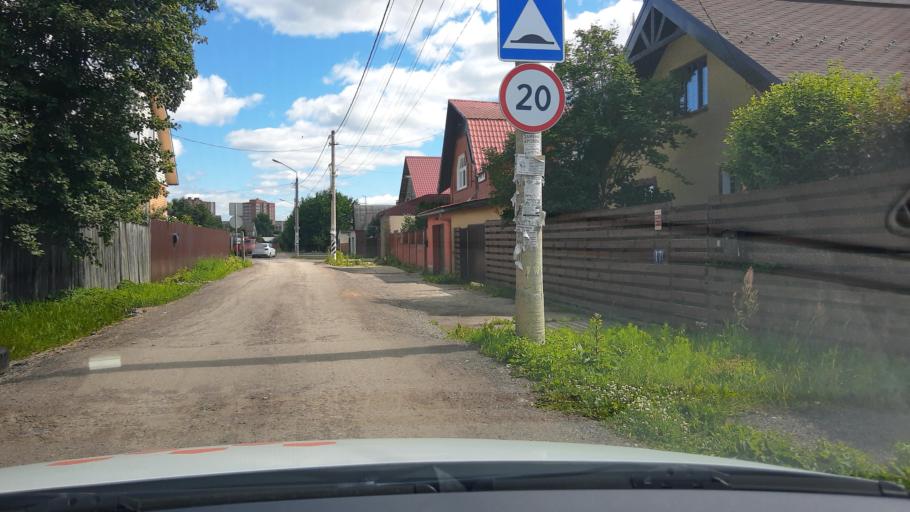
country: RU
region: Moskovskaya
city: Noginsk
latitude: 55.8699
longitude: 38.4264
